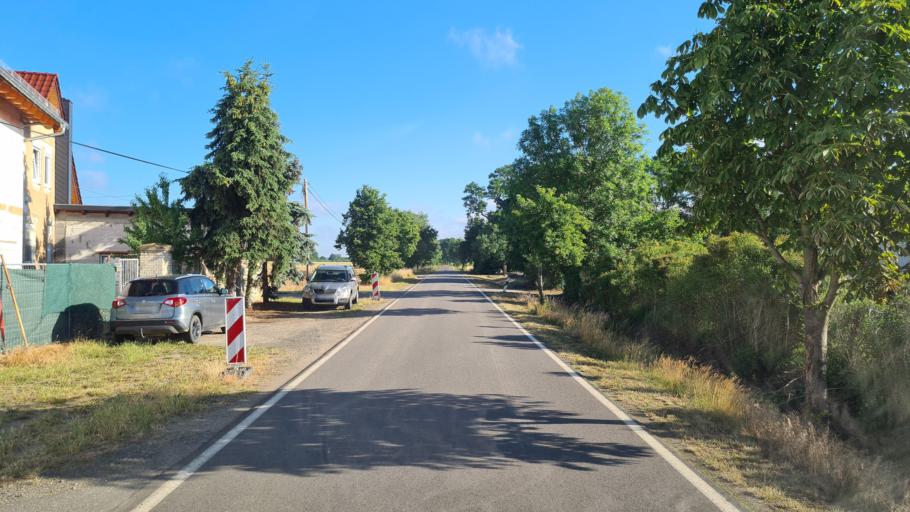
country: DE
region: Saxony
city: Beilrode
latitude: 51.6074
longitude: 13.1233
